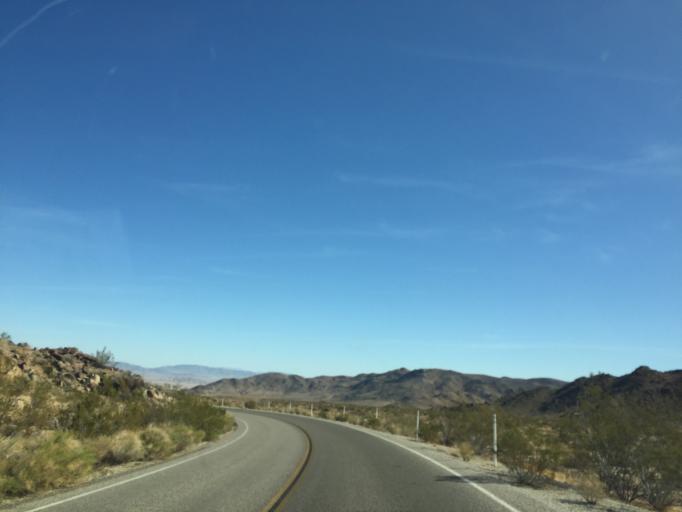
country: US
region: California
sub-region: San Bernardino County
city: Twentynine Palms
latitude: 34.0561
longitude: -116.0257
